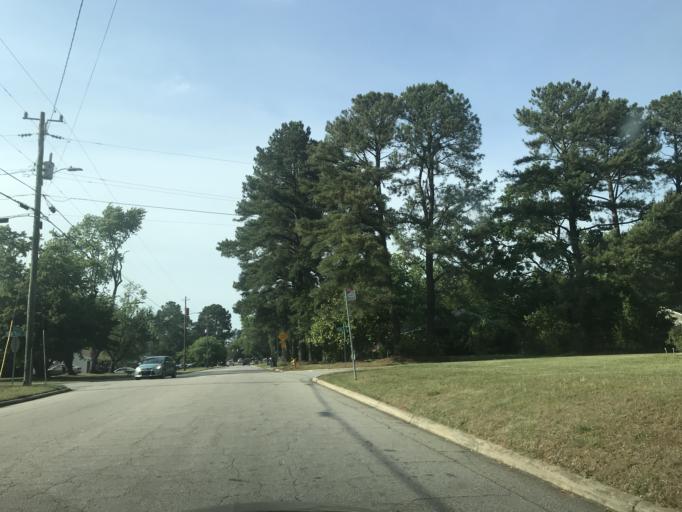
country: US
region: North Carolina
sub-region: Wake County
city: Raleigh
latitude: 35.7691
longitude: -78.5945
